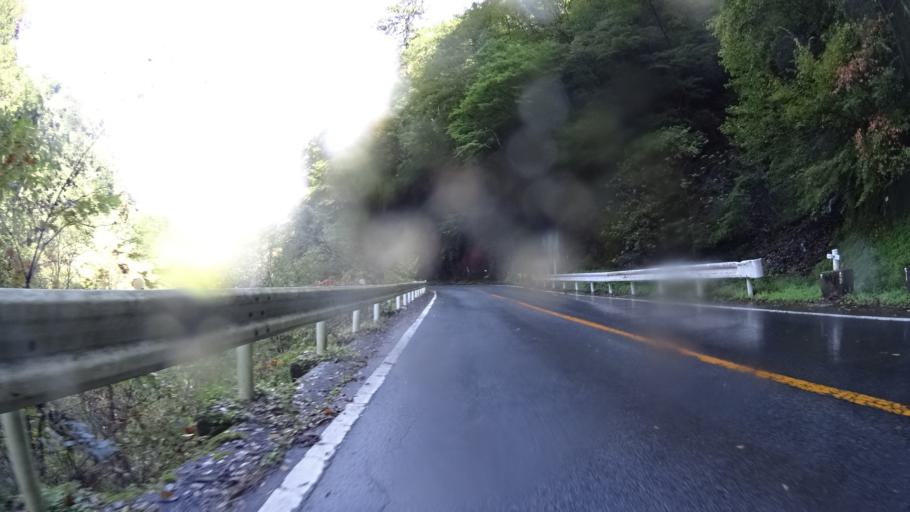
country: JP
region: Yamanashi
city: Enzan
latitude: 35.7965
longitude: 138.8660
